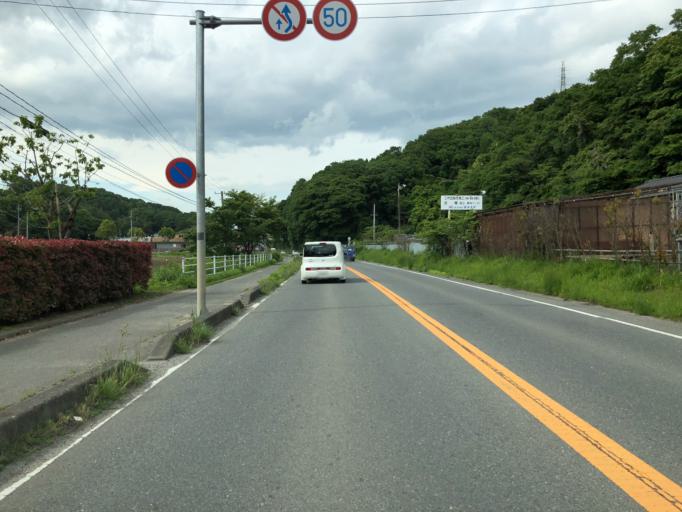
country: JP
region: Fukushima
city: Iwaki
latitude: 36.9629
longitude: 140.8718
